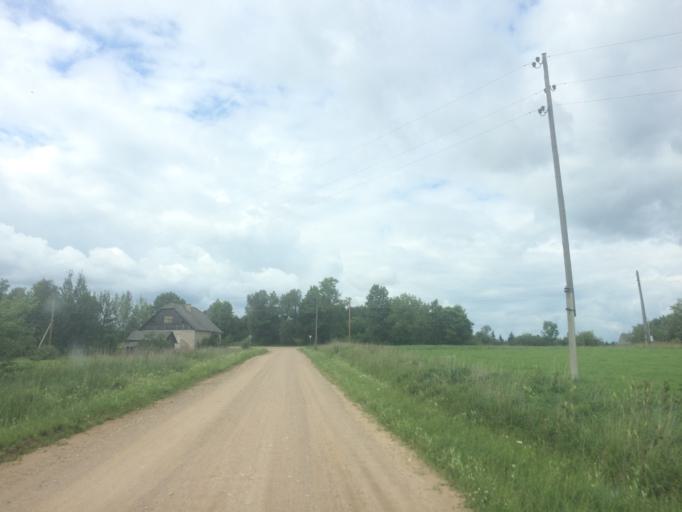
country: LV
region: Rezekne
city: Rezekne
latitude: 56.6619
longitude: 27.2699
